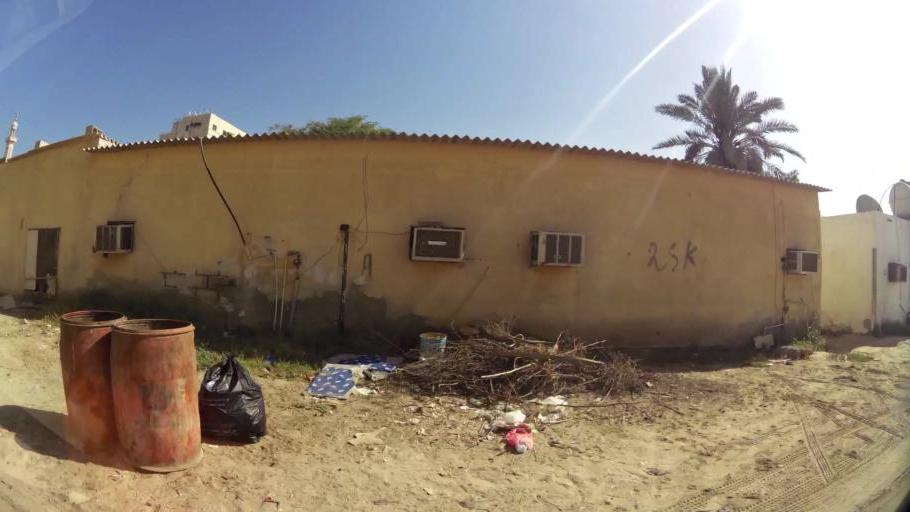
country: AE
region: Ajman
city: Ajman
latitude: 25.4135
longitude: 55.4473
